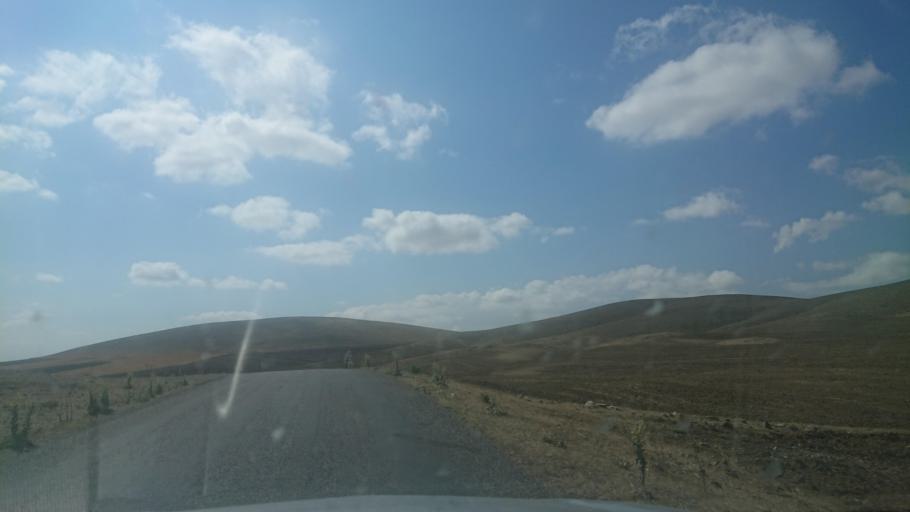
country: TR
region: Aksaray
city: Sariyahsi
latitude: 39.0048
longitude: 33.9603
